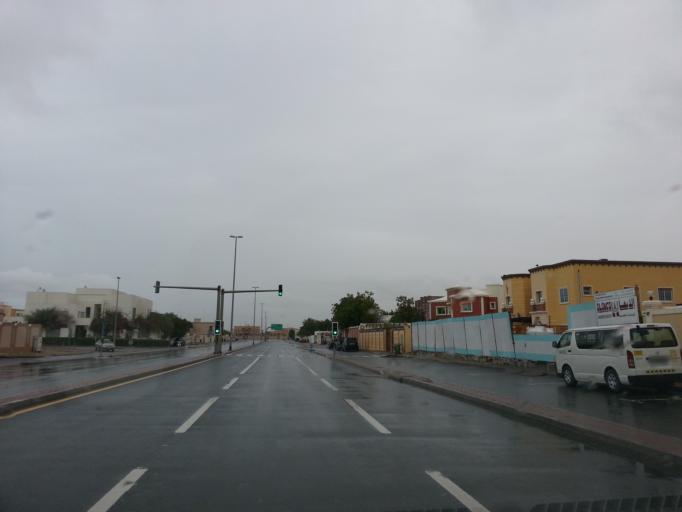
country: AE
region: Dubai
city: Dubai
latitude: 25.0903
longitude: 55.2013
